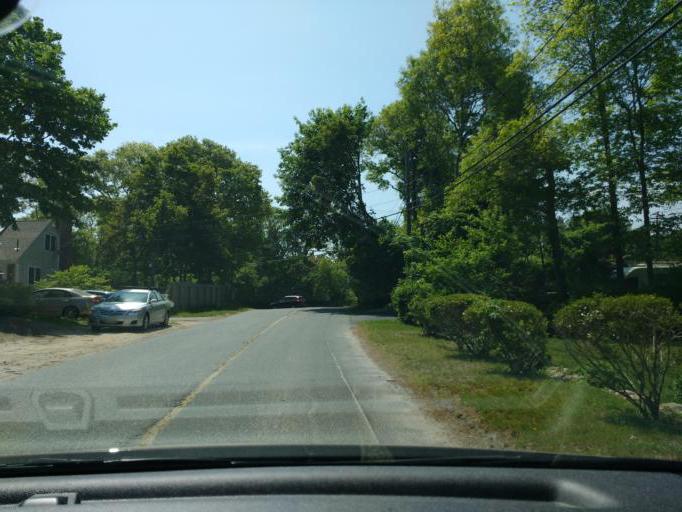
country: US
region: Massachusetts
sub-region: Barnstable County
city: East Falmouth
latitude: 41.5974
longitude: -70.5748
